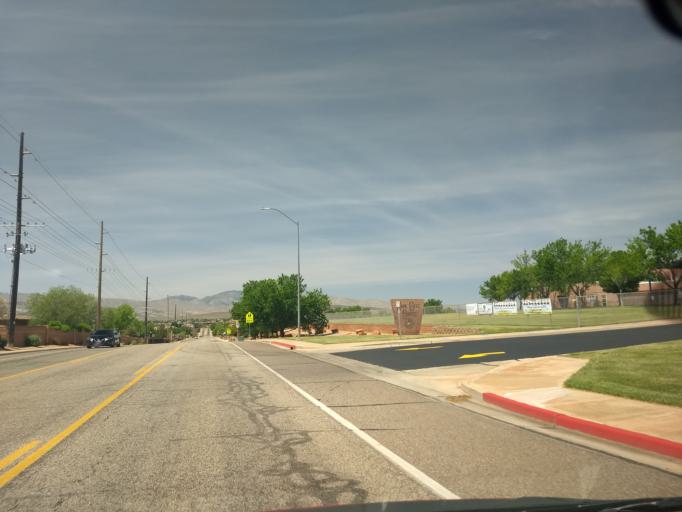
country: US
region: Utah
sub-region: Washington County
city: Santa Clara
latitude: 37.1431
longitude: -113.6266
